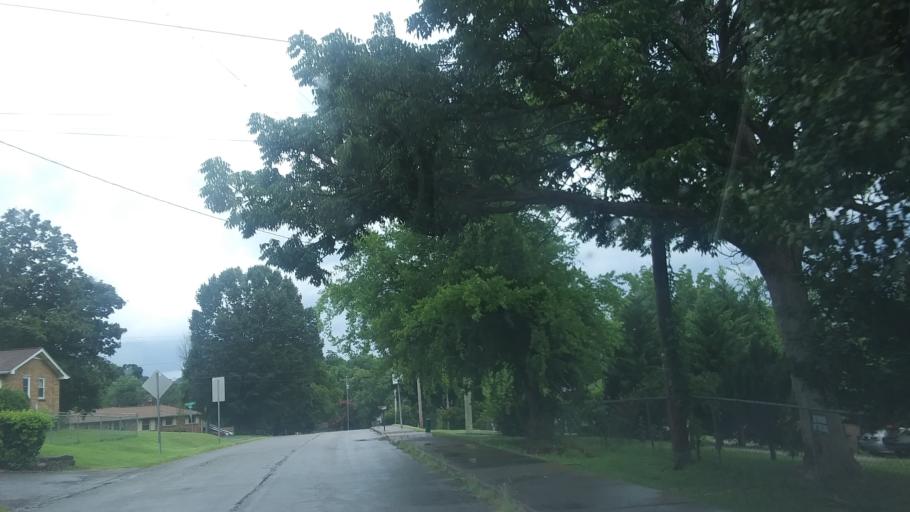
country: US
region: Tennessee
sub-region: Davidson County
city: Belle Meade
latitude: 36.1532
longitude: -86.8828
